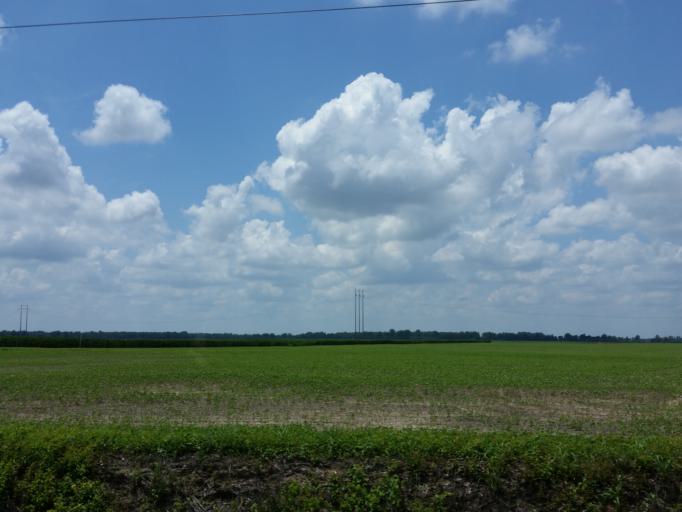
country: US
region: Tennessee
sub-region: Lake County
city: Ridgely
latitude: 36.2041
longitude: -89.4604
